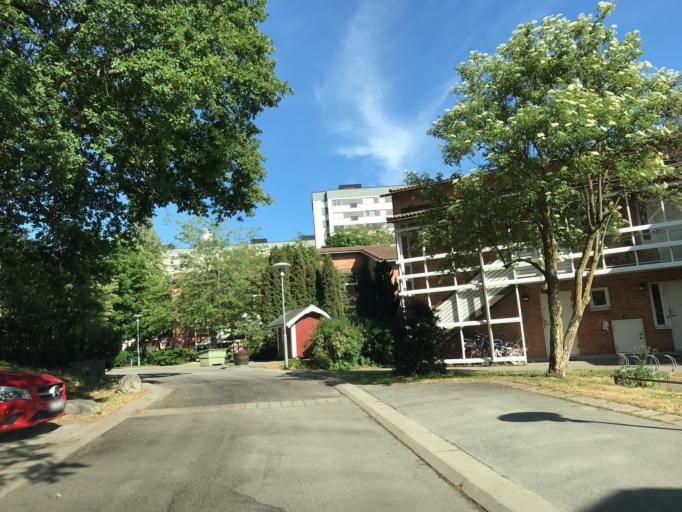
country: SE
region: Stockholm
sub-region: Huddinge Kommun
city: Segeltorp
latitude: 59.2969
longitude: 17.9360
